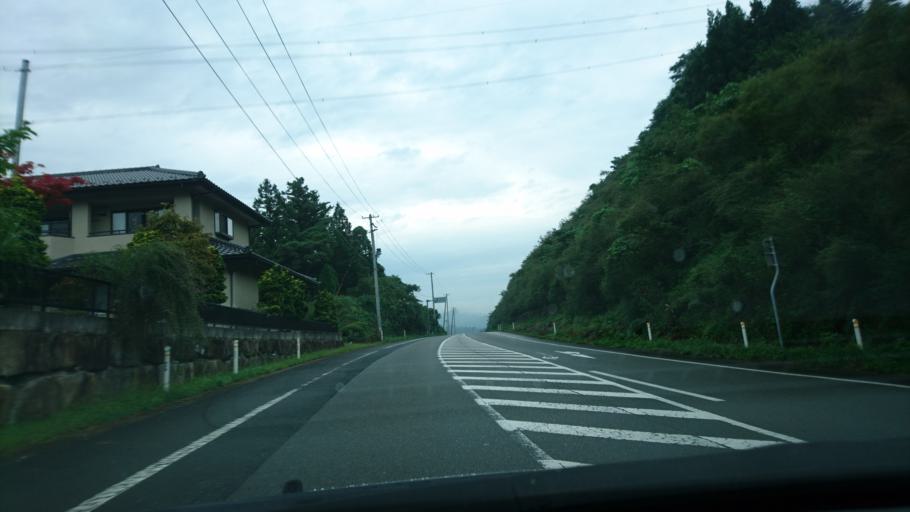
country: JP
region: Iwate
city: Ichinoseki
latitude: 38.9352
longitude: 141.2496
